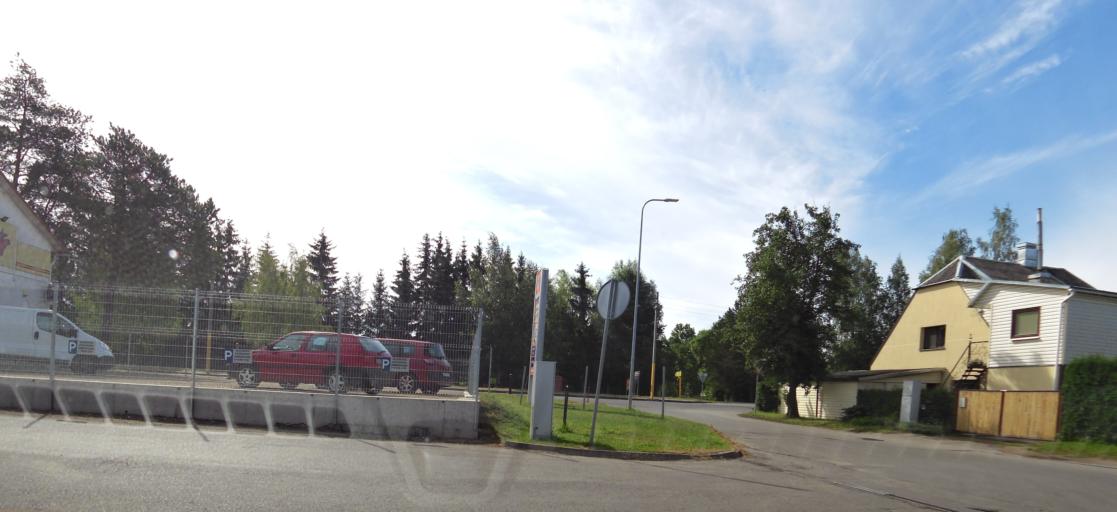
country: LT
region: Panevezys
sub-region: Birzai
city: Birzai
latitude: 56.2076
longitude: 24.7707
